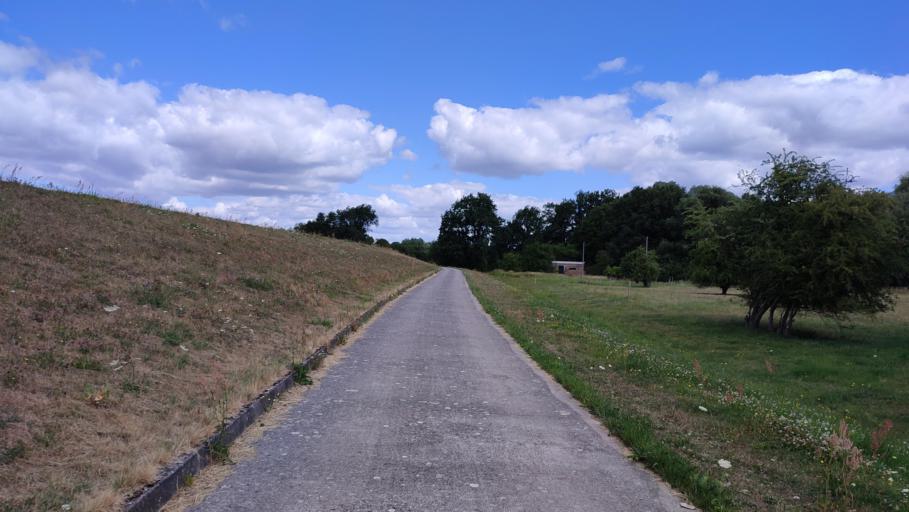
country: DE
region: Lower Saxony
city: Hitzacker
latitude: 53.1988
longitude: 10.9806
